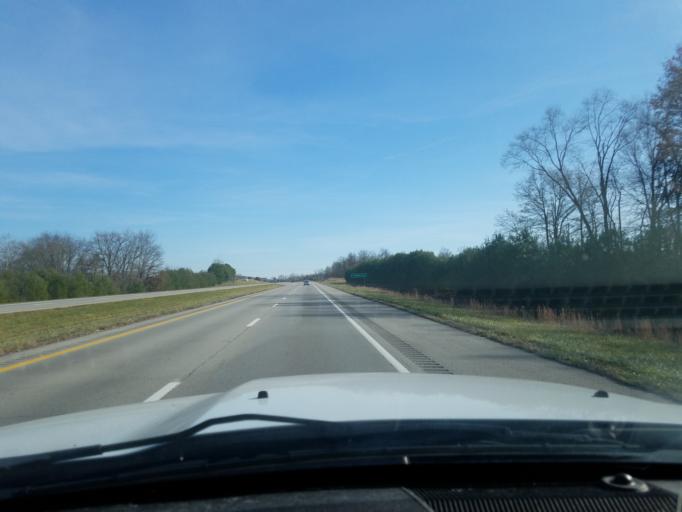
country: US
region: Ohio
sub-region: Pike County
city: Piketon
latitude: 39.0527
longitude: -82.9509
